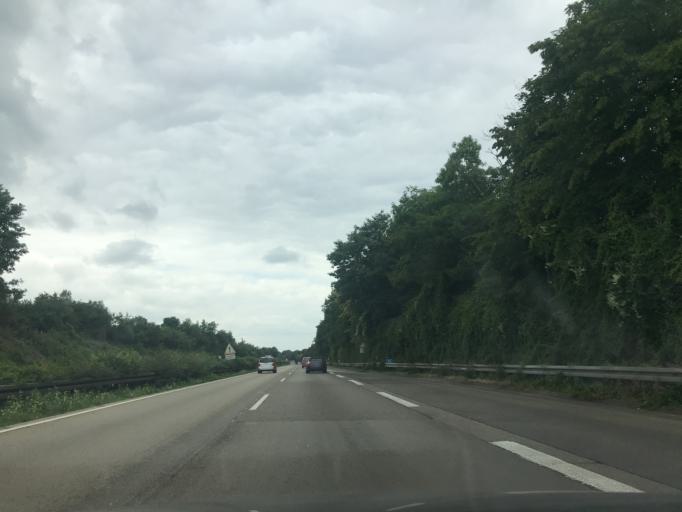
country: DE
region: North Rhine-Westphalia
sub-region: Regierungsbezirk Dusseldorf
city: Hilden
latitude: 51.1555
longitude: 6.8910
